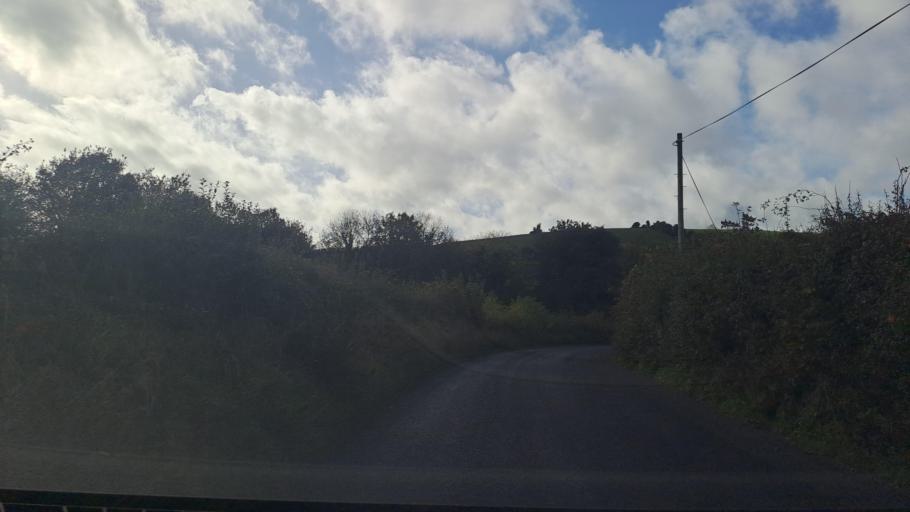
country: IE
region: Ulster
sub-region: An Cabhan
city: Cootehill
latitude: 54.0336
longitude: -7.0060
